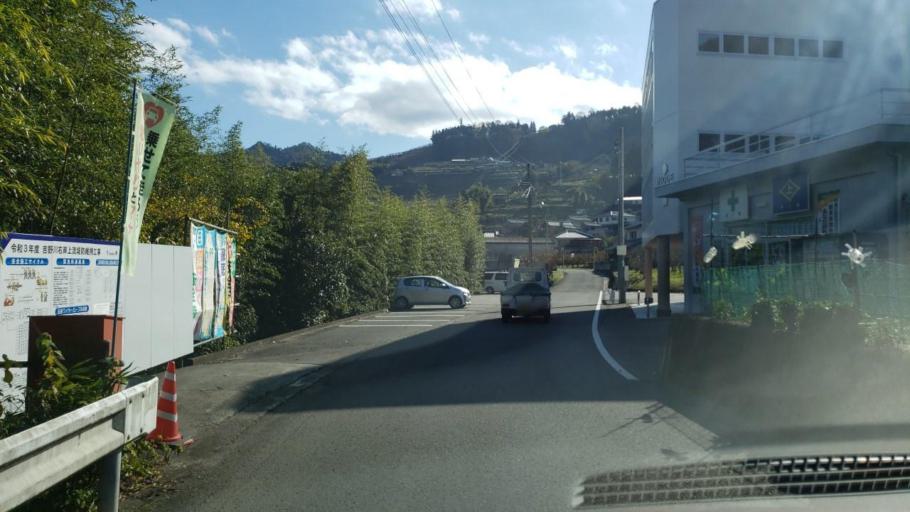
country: JP
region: Tokushima
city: Wakimachi
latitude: 34.0263
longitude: 134.0294
